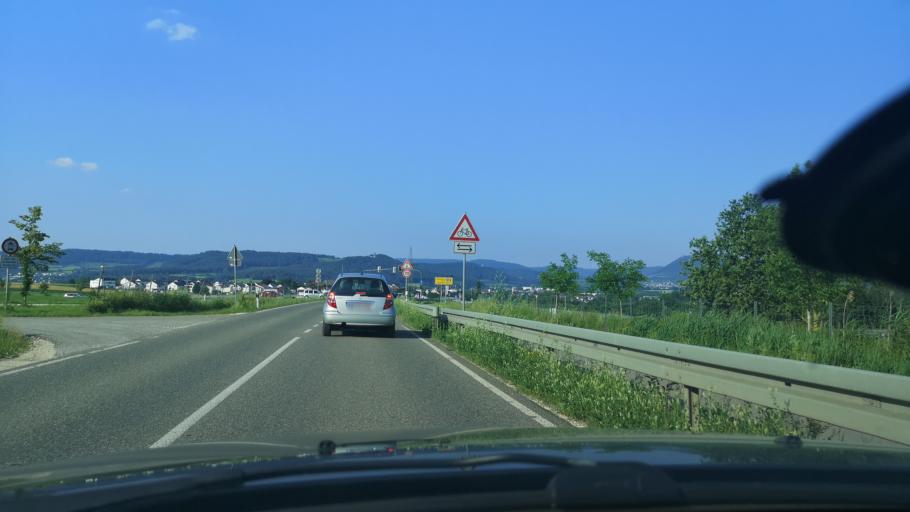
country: DE
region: Baden-Wuerttemberg
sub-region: Regierungsbezirk Stuttgart
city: Salach
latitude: 48.6685
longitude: 9.7305
